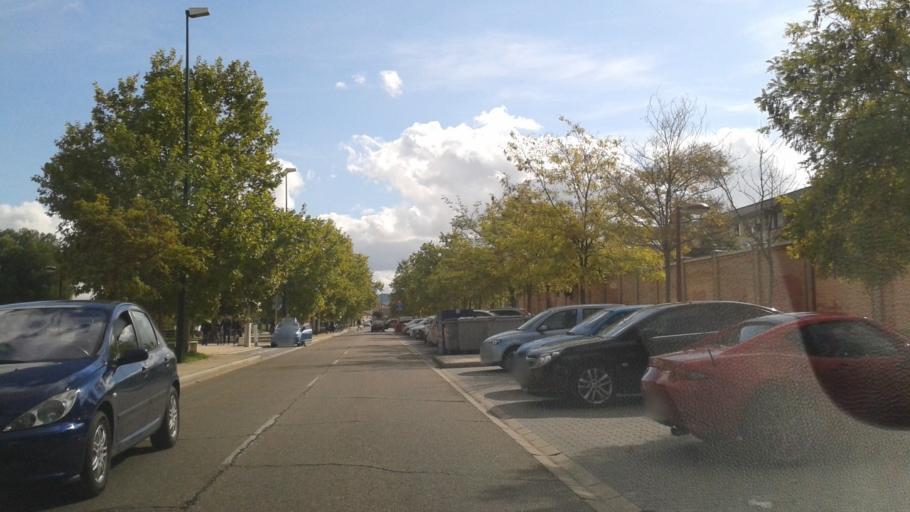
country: ES
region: Castille and Leon
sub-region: Provincia de Valladolid
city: Valladolid
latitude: 41.6623
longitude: -4.7087
